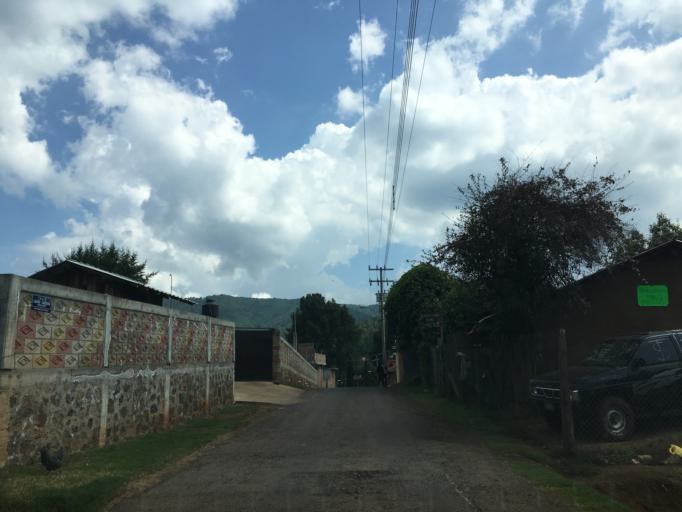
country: MX
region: Michoacan
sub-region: Morelia
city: Montana Monarca (Punta Altozano)
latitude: 19.5843
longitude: -101.1891
